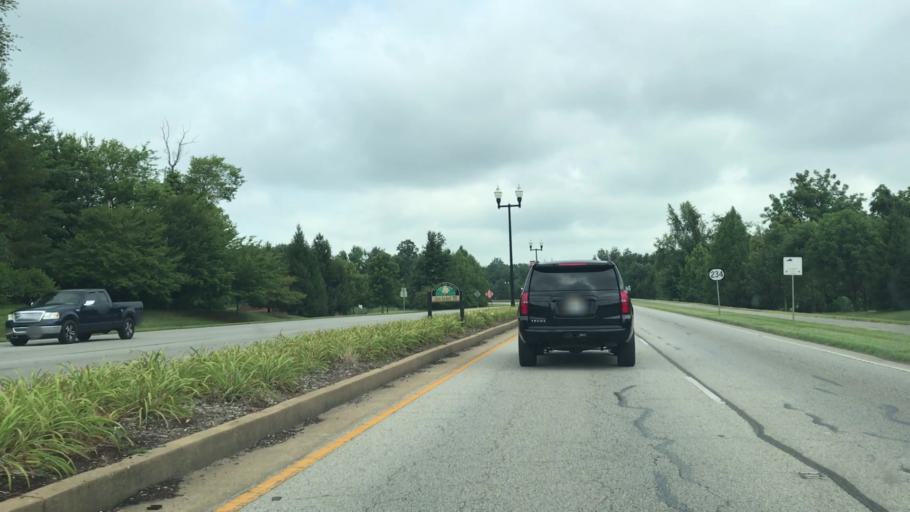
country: US
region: Kentucky
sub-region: Warren County
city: Bowling Green
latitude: 36.9819
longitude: -86.3964
